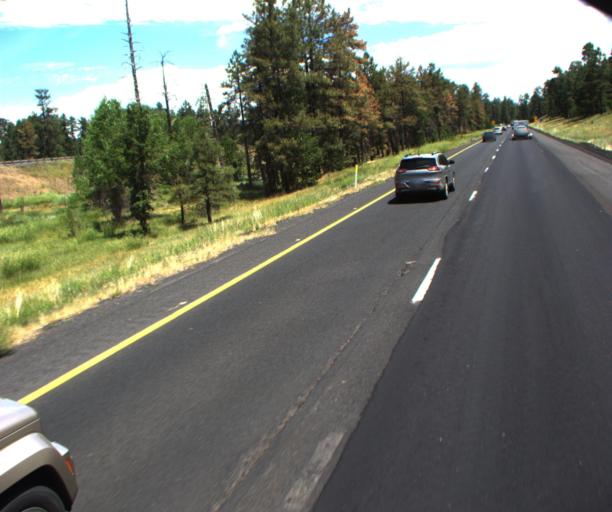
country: US
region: Arizona
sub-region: Coconino County
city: Sedona
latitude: 34.8285
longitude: -111.6075
